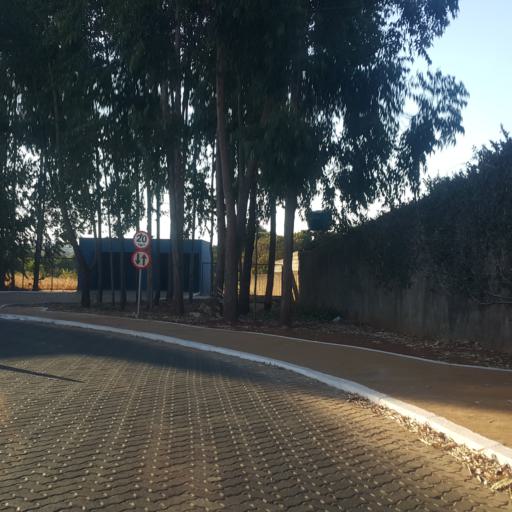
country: BR
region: Federal District
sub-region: Brasilia
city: Brasilia
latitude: -15.8271
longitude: -48.0115
